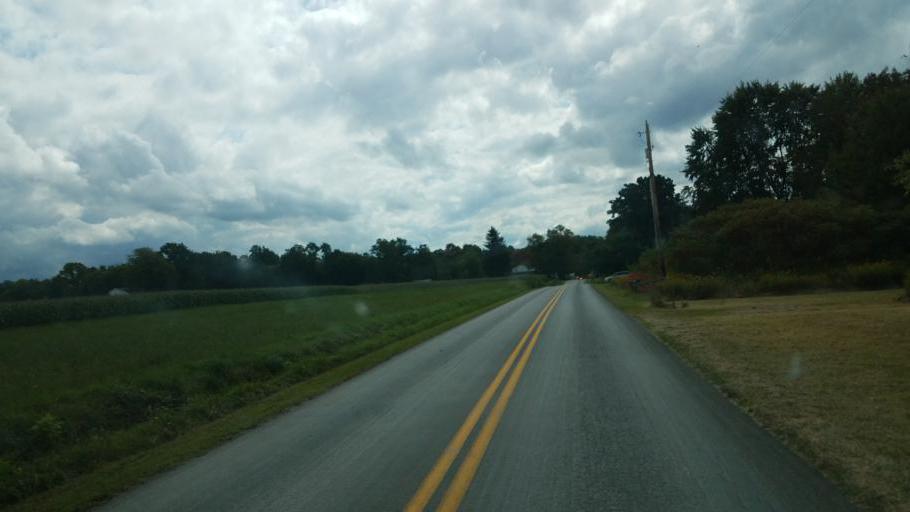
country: US
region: Pennsylvania
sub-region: Mercer County
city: Greenville
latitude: 41.4871
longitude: -80.3386
